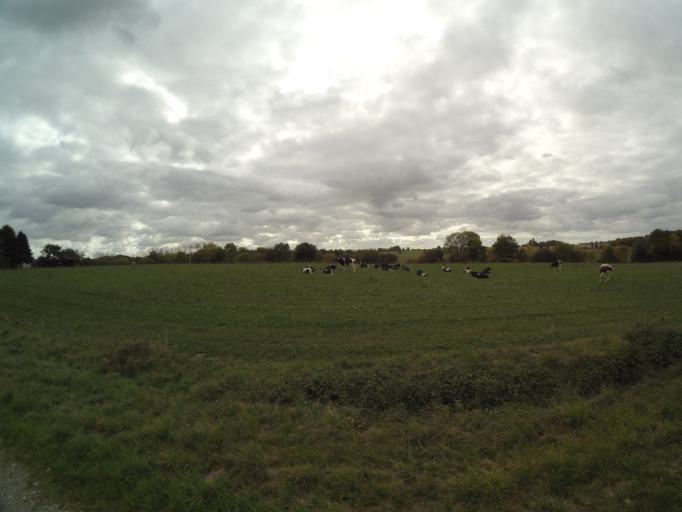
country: FR
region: Pays de la Loire
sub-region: Departement de la Loire-Atlantique
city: Remouille
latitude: 47.0487
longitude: -1.3470
